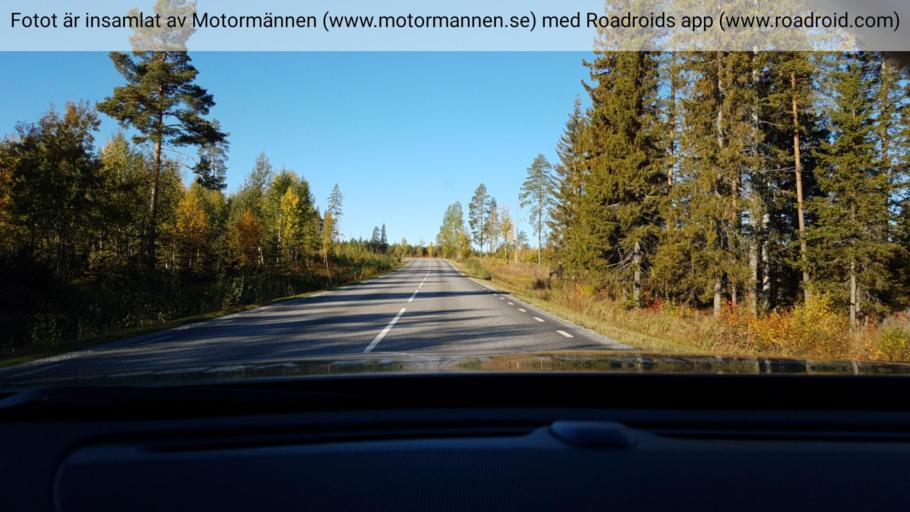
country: SE
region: Norrbotten
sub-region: Pitea Kommun
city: Roknas
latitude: 65.3581
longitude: 21.0588
